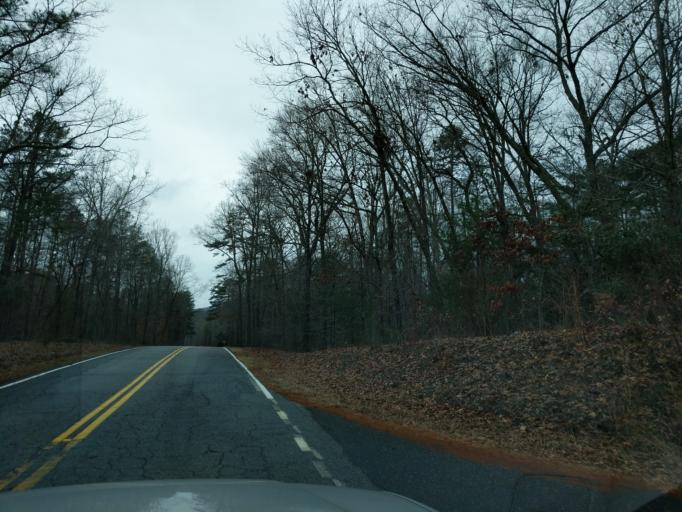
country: US
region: South Carolina
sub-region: Oconee County
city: Walhalla
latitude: 34.7925
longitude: -83.1000
